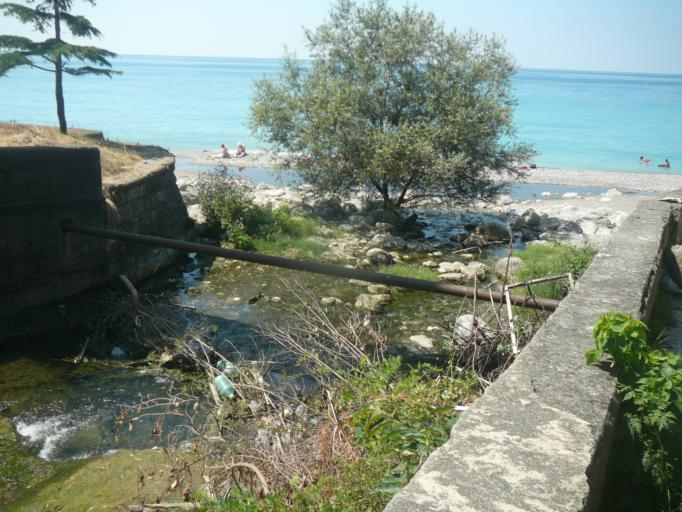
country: GE
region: Abkhazia
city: Gagra
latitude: 43.3159
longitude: 40.2456
